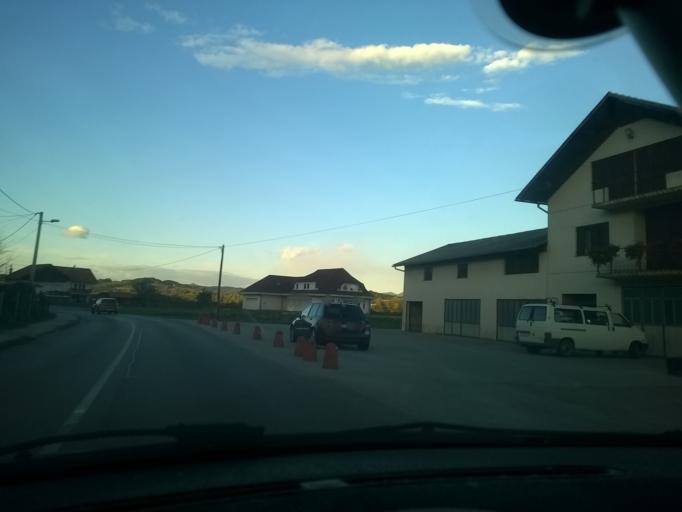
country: HR
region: Krapinsko-Zagorska
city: Zabok
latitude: 46.0587
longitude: 15.9103
